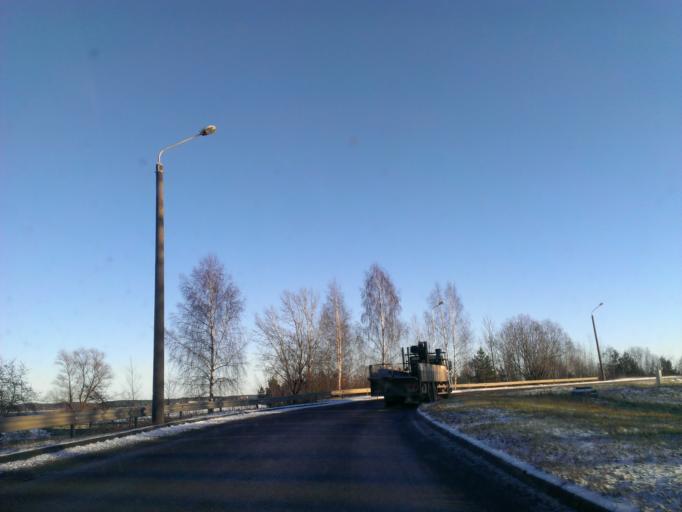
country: LV
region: Riga
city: Jaunciems
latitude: 57.0324
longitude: 24.1342
